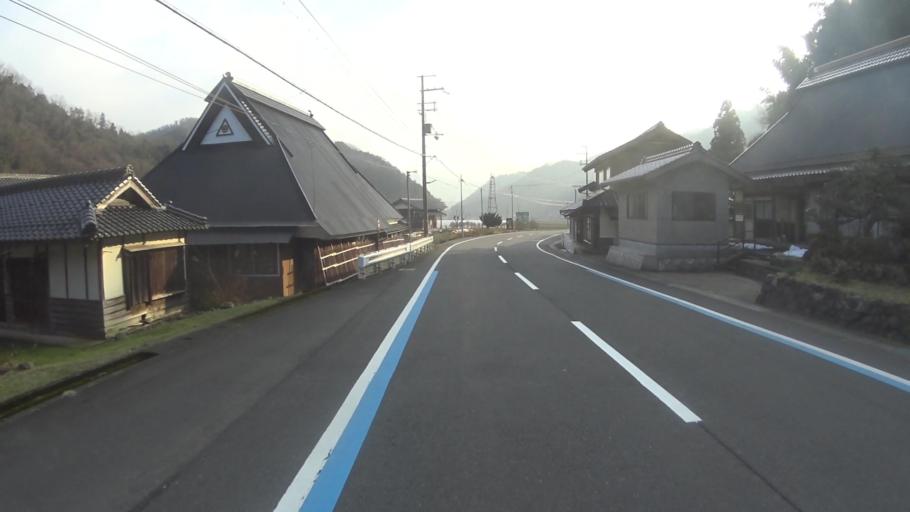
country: JP
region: Kyoto
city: Maizuru
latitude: 35.4001
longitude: 135.4153
